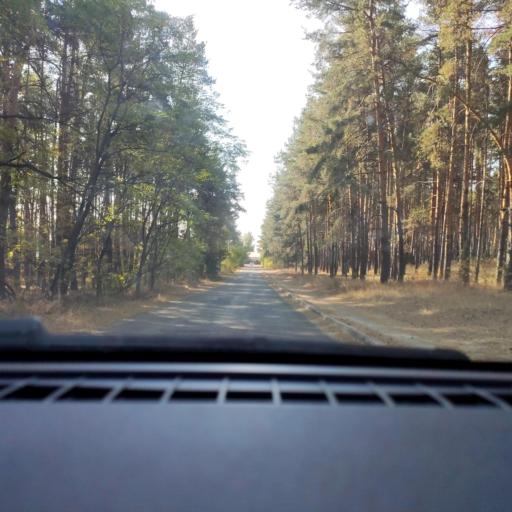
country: RU
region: Voronezj
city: Maslovka
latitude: 51.5488
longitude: 39.2213
